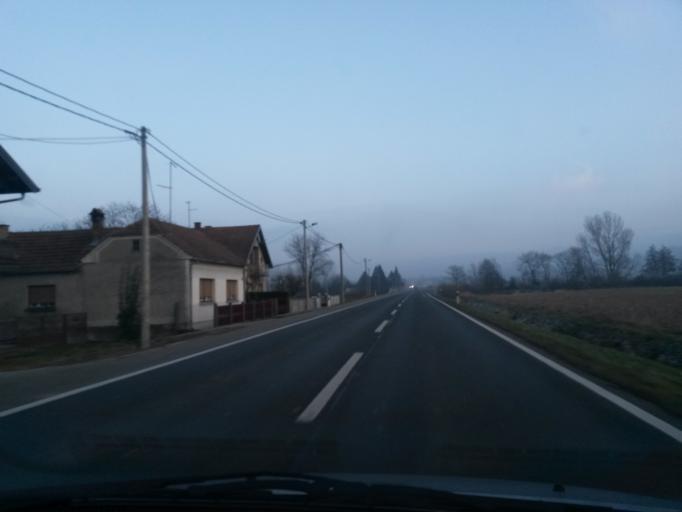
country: HR
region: Koprivnicko-Krizevacka
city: Reka
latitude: 46.1967
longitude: 16.7221
